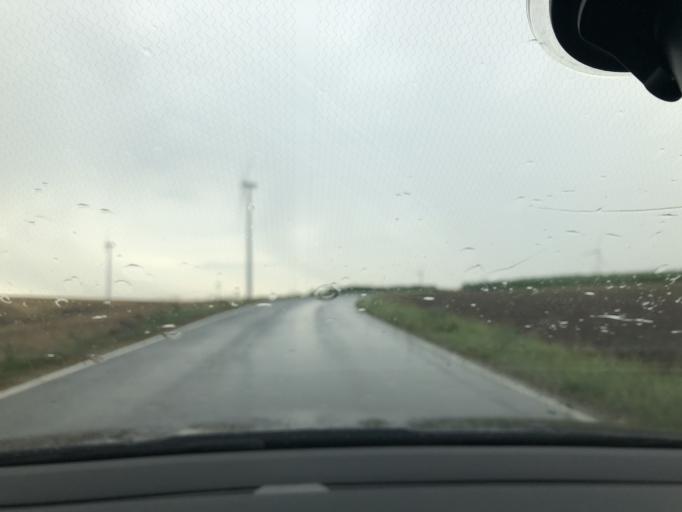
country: AT
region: Lower Austria
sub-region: Politischer Bezirk Ganserndorf
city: Auersthal
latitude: 48.3600
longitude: 16.6710
